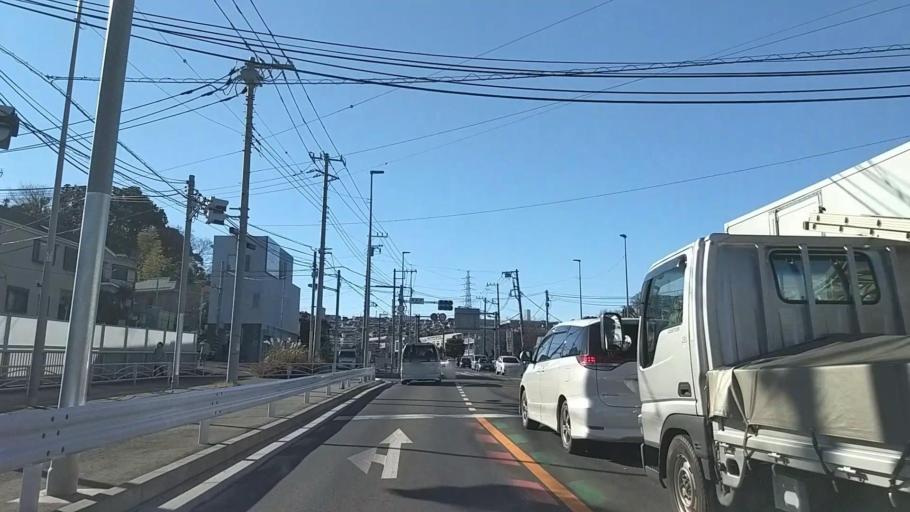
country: JP
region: Kanagawa
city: Yokohama
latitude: 35.3793
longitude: 139.6222
